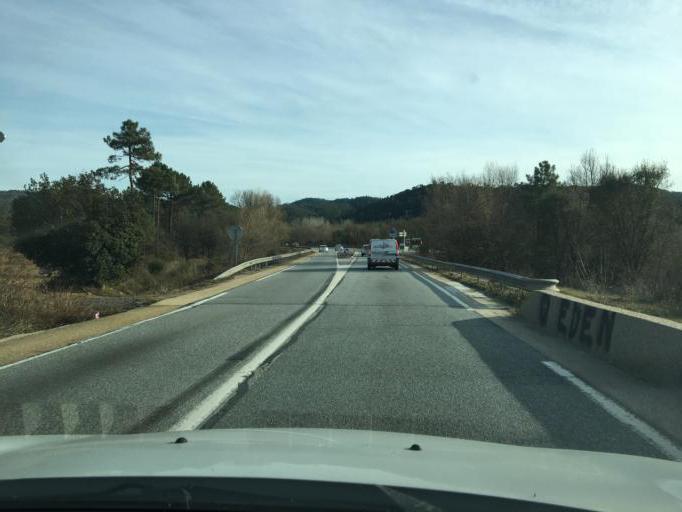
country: FR
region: Provence-Alpes-Cote d'Azur
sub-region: Departement du Var
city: Montauroux
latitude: 43.5536
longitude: 6.7959
